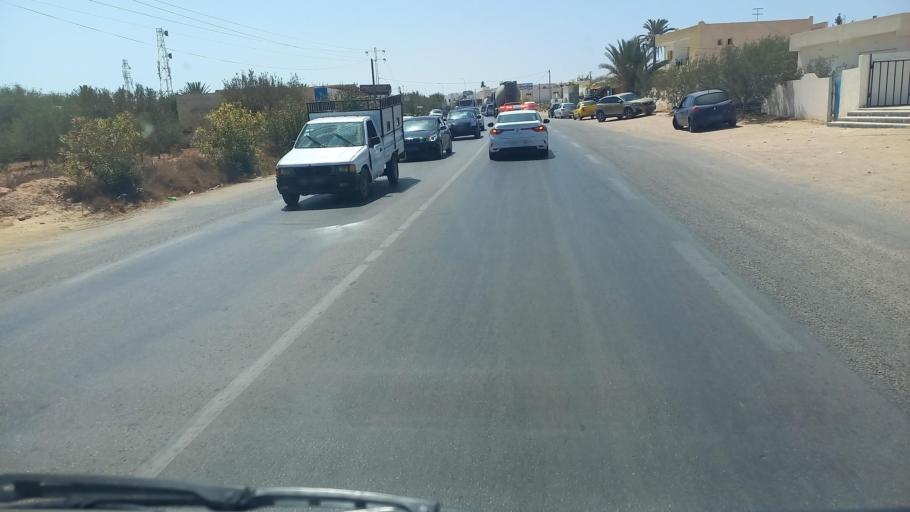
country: TN
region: Madanin
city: Houmt Souk
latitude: 33.8070
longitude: 10.8811
